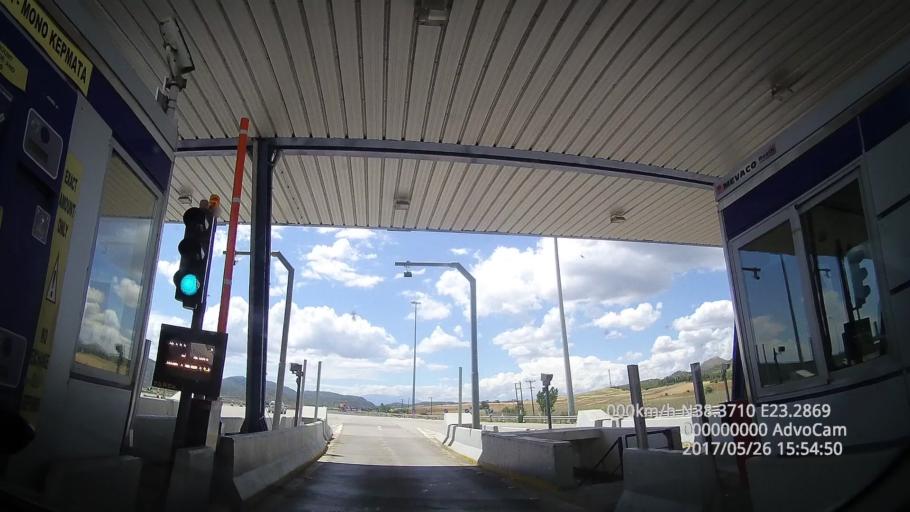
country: GR
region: Central Greece
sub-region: Nomos Fthiotidos
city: Ayios Konstandinos
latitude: 38.7519
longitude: 22.9066
